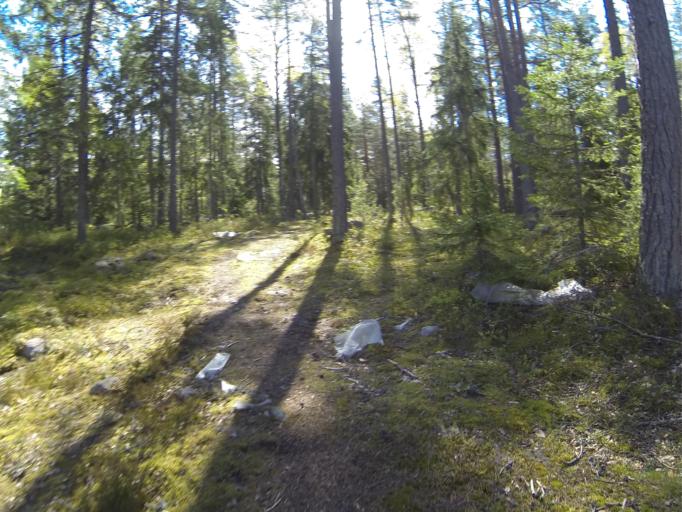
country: FI
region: Varsinais-Suomi
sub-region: Salo
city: Salo
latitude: 60.3972
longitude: 23.1960
